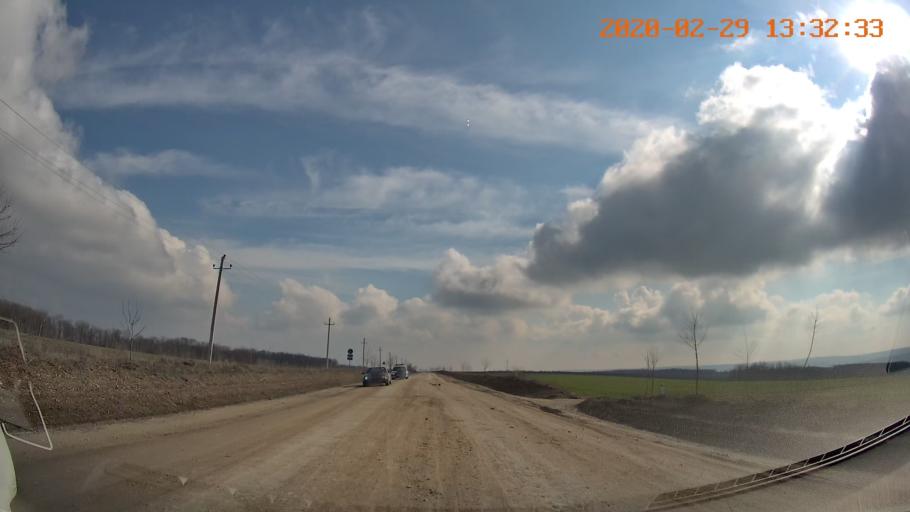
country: MD
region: Telenesti
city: Camenca
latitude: 47.8783
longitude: 28.6107
